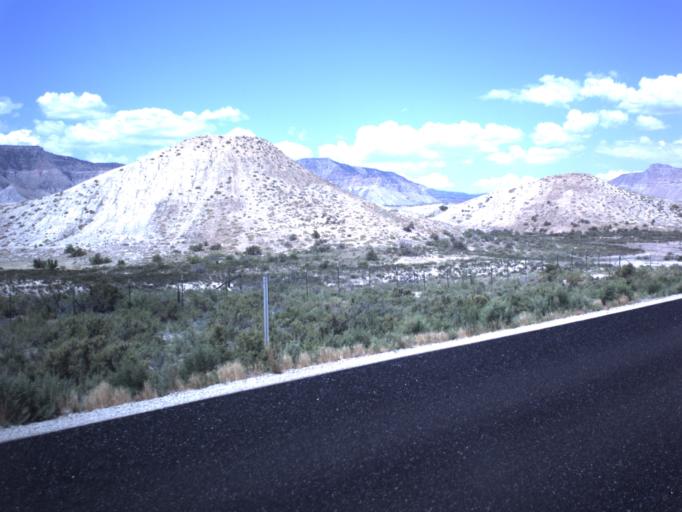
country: US
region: Utah
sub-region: Emery County
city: Ferron
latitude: 39.0553
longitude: -111.1255
